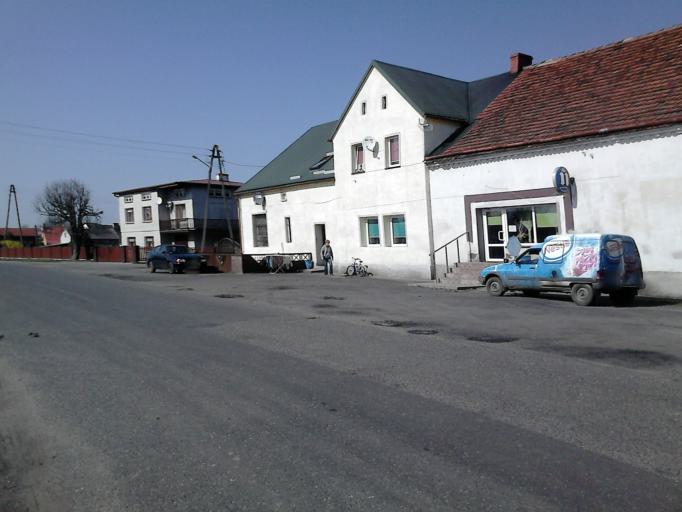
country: PL
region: Lower Silesian Voivodeship
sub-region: Powiat olesnicki
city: Dziadowa Kloda
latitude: 51.1779
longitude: 17.6872
